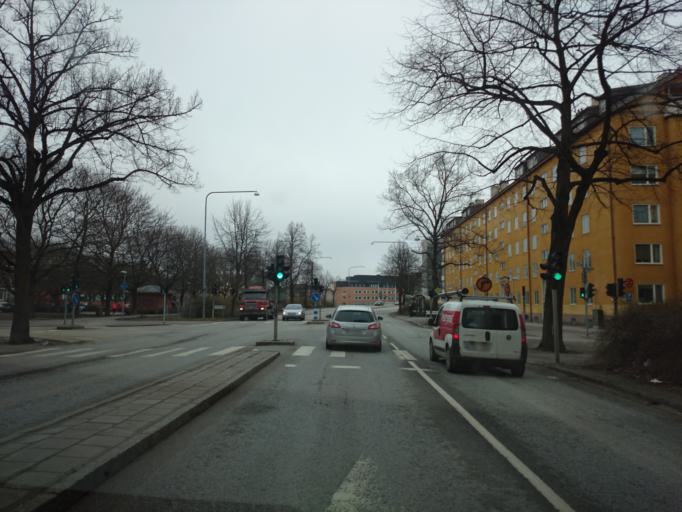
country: SE
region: Uppsala
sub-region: Uppsala Kommun
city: Uppsala
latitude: 59.8640
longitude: 17.6263
